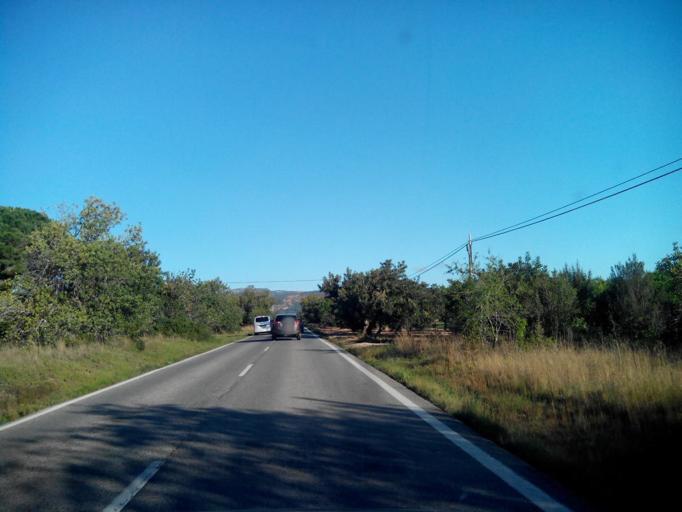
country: ES
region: Catalonia
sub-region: Provincia de Tarragona
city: Riudecanyes
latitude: 41.0689
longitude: 0.9814
